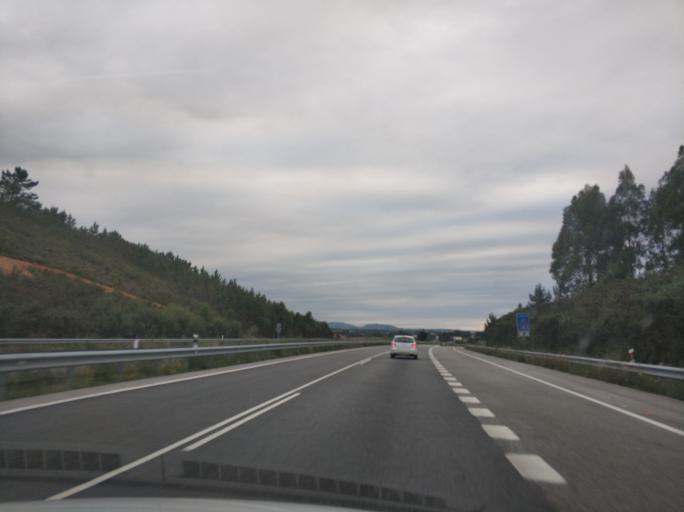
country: ES
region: Asturias
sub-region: Province of Asturias
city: Tineo
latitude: 43.5453
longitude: -6.4420
